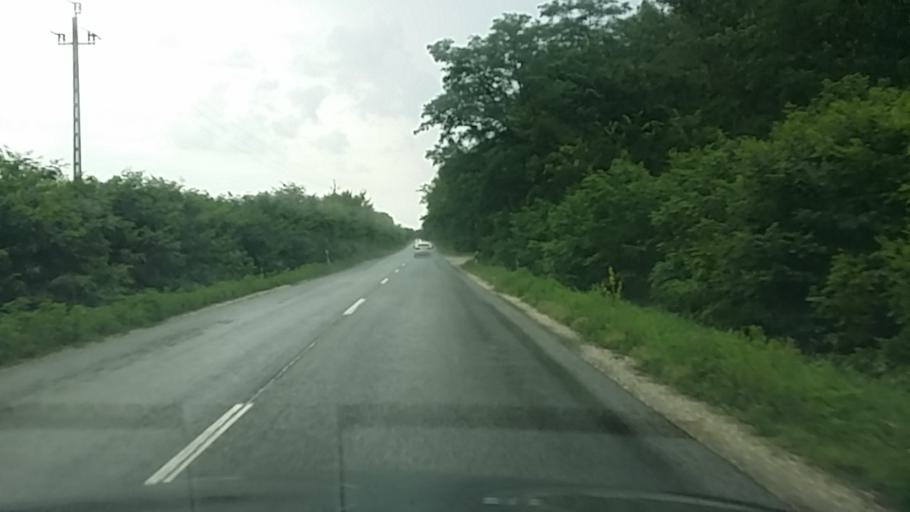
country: HU
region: Pest
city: Ullo
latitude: 47.3351
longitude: 19.3183
